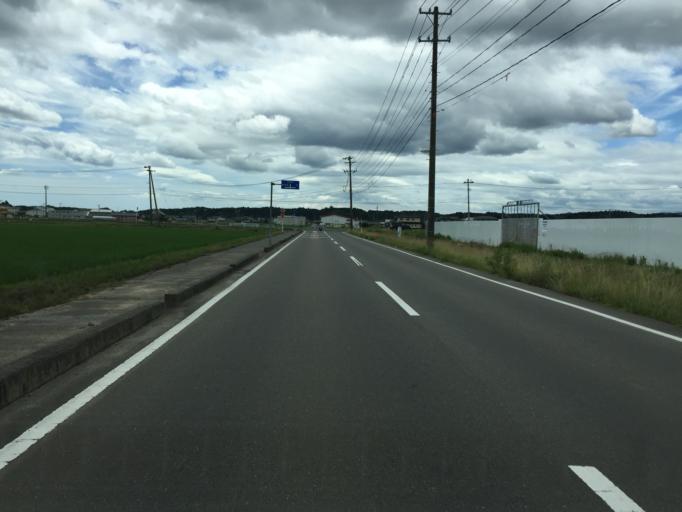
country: JP
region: Fukushima
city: Namie
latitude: 37.7079
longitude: 140.9719
